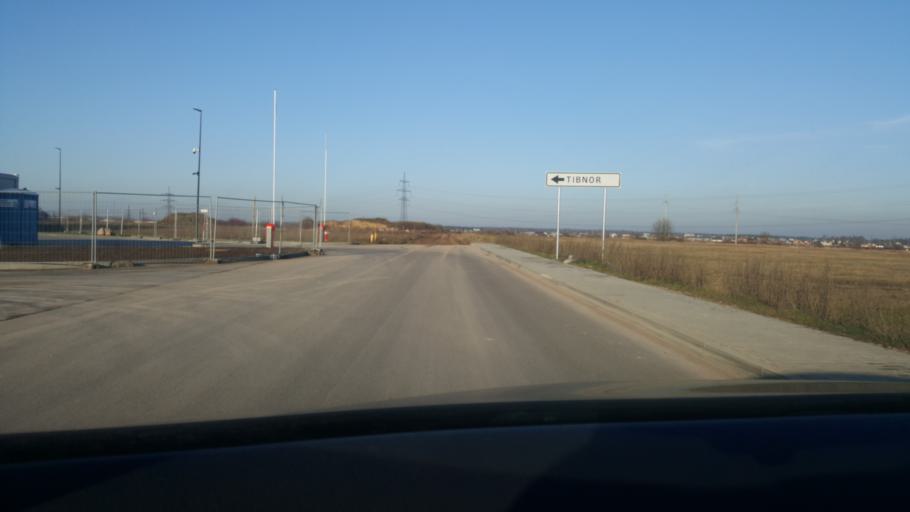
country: LT
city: Ramuciai
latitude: 54.9332
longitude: 24.0346
